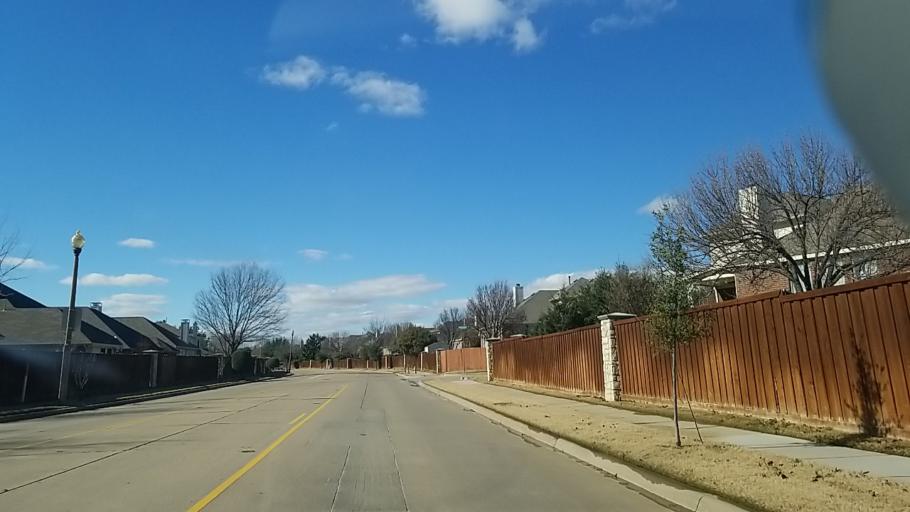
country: US
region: Texas
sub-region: Denton County
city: Denton
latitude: 33.1769
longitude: -97.1061
